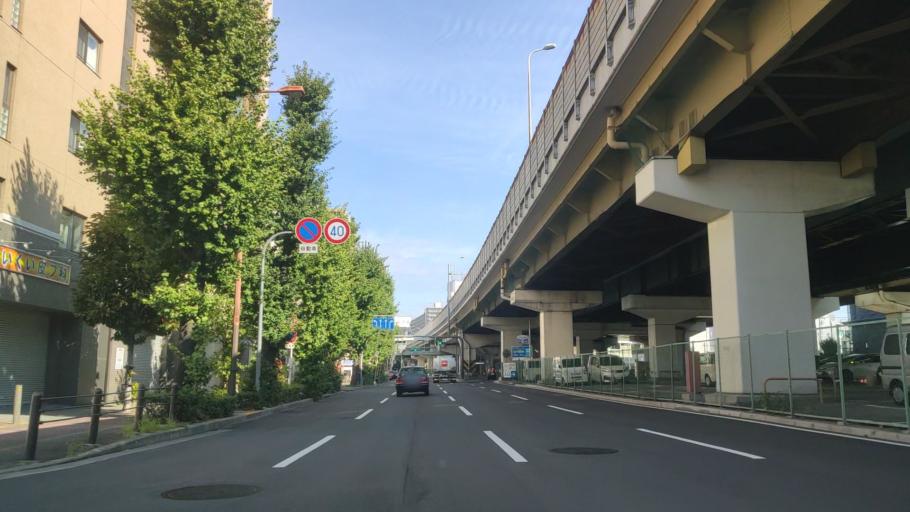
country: JP
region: Osaka
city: Suita
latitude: 34.7406
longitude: 135.4984
